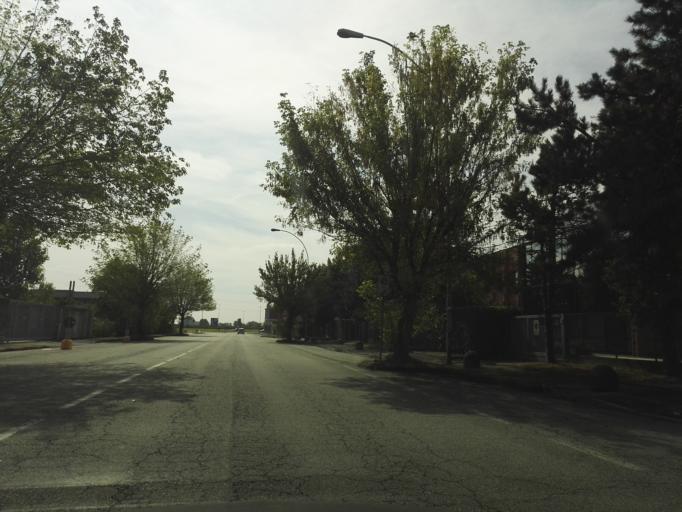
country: IT
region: Lombardy
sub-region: Citta metropolitana di Milano
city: Bettola-Zeloforomagno
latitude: 45.4307
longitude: 9.3240
